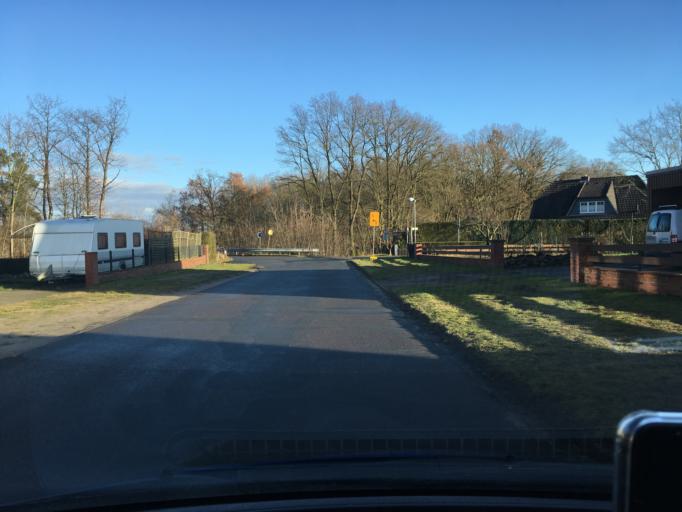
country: DE
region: Lower Saxony
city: Wendisch Evern
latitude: 53.2176
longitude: 10.4769
